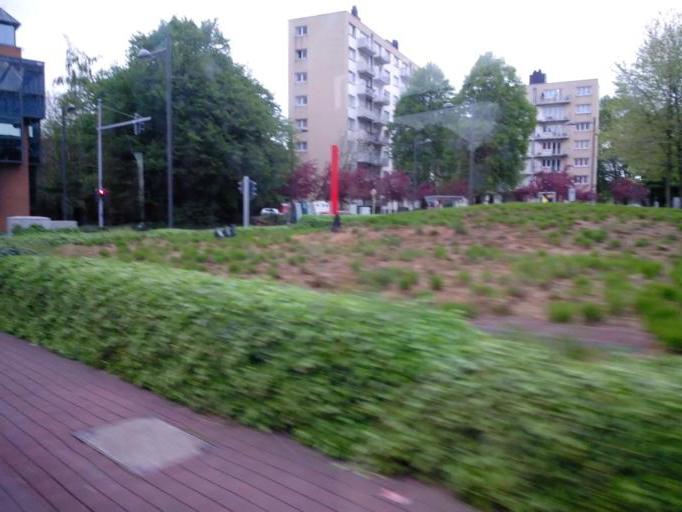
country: BE
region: Flanders
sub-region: Provincie Vlaams-Brabant
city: Diegem
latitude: 50.8572
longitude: 4.4084
